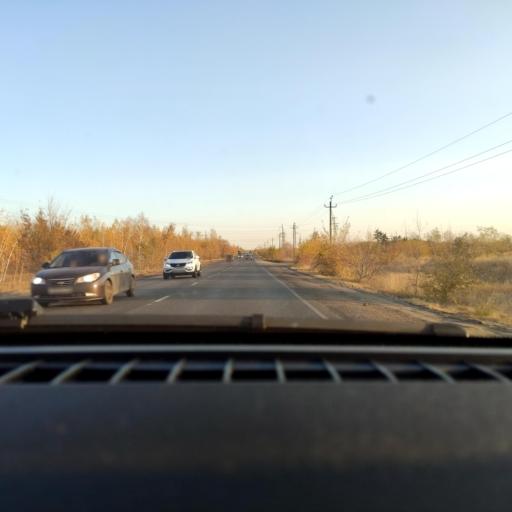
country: RU
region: Voronezj
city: Maslovka
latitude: 51.5852
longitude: 39.2567
